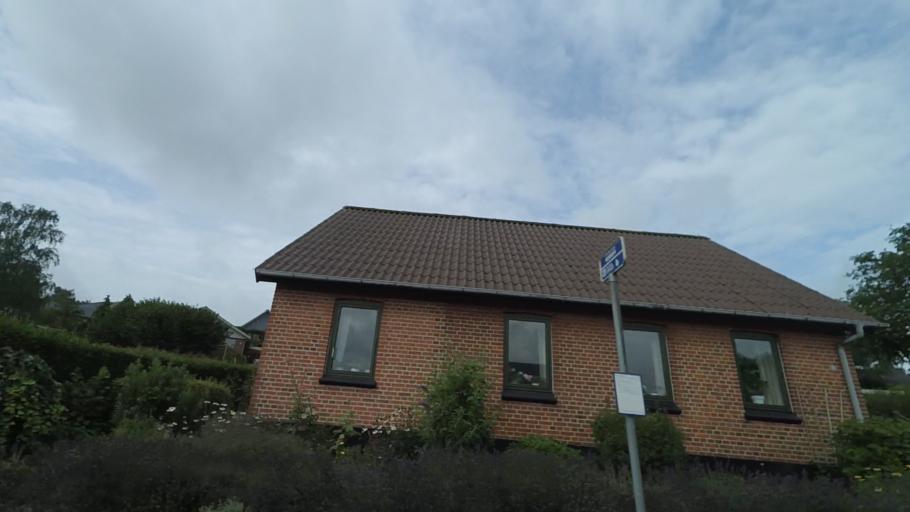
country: DK
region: Central Jutland
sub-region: Syddjurs Kommune
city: Ronde
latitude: 56.3406
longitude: 10.4636
